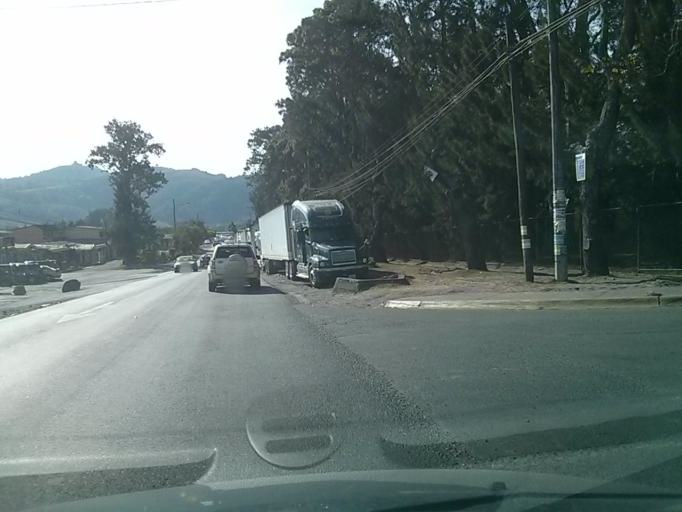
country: CR
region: Cartago
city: Cartago
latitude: 9.8791
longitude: -83.9307
